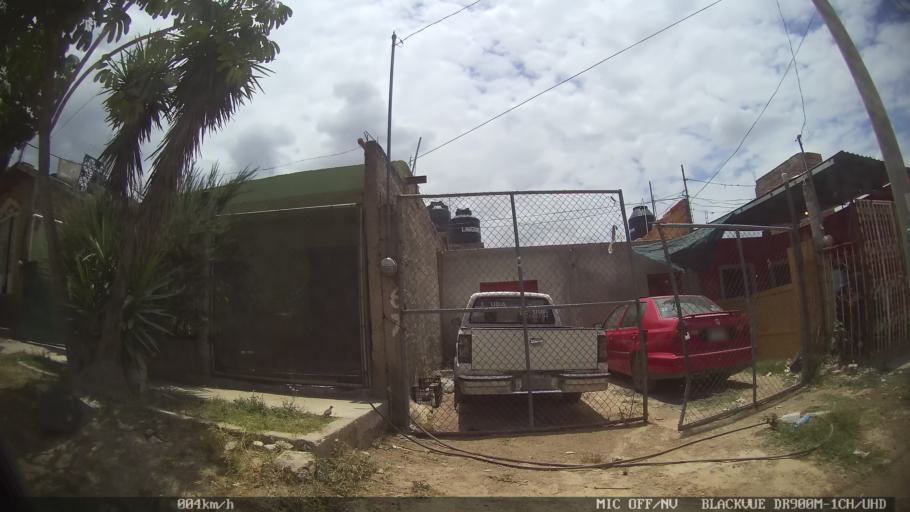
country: MX
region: Jalisco
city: Tlaquepaque
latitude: 20.6419
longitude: -103.2677
